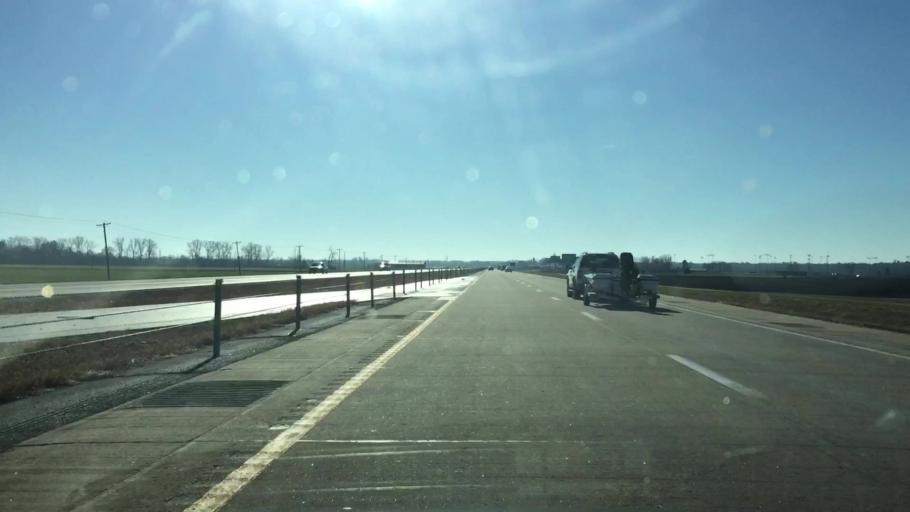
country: US
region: Missouri
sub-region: Cole County
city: Jefferson City
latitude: 38.6285
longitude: -92.1953
